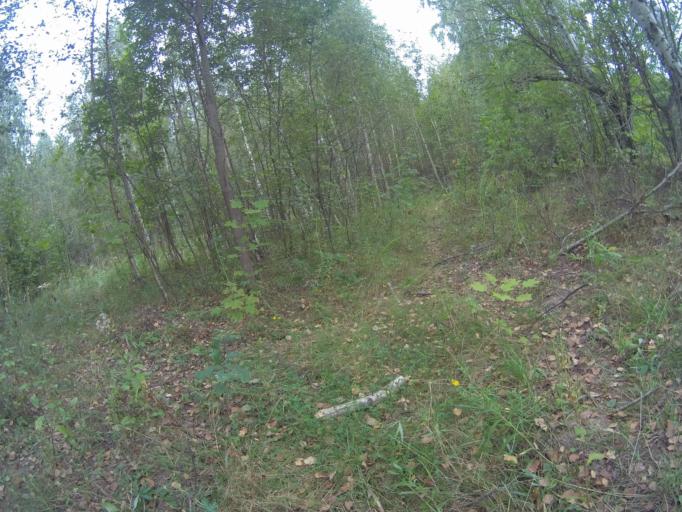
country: RU
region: Vladimir
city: Golovino
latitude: 55.9968
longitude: 40.5013
